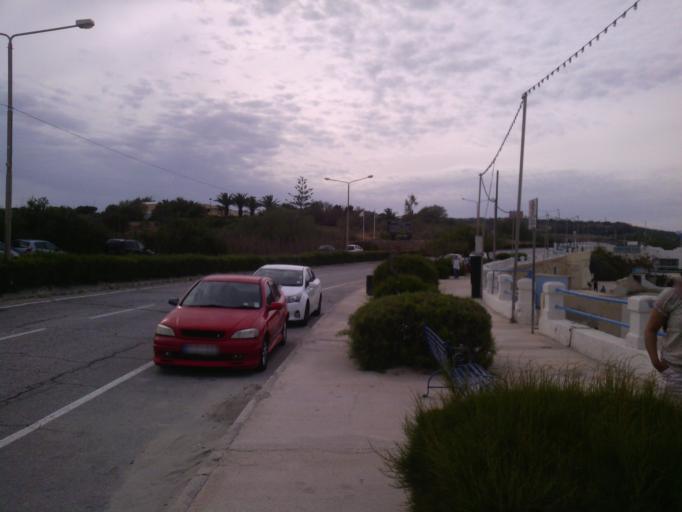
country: MT
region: Il-Mellieha
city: Mellieha
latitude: 35.9664
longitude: 14.3527
